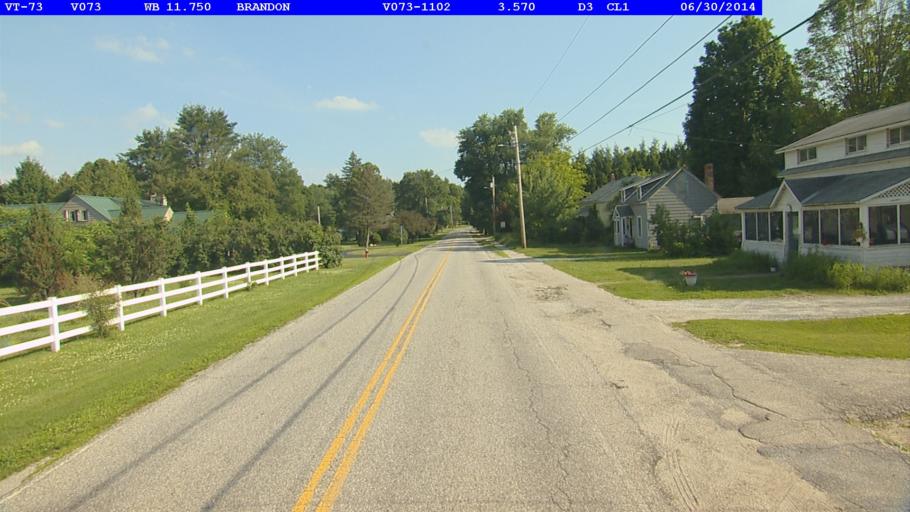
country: US
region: Vermont
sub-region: Rutland County
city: Brandon
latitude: 43.8015
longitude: -73.0805
